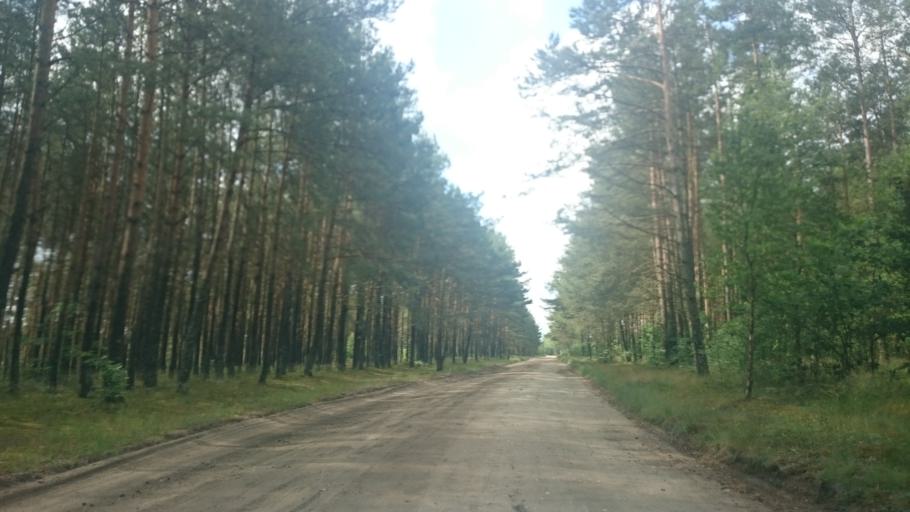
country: PL
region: Pomeranian Voivodeship
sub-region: Powiat koscierski
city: Karsin
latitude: 53.9787
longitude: 17.9326
